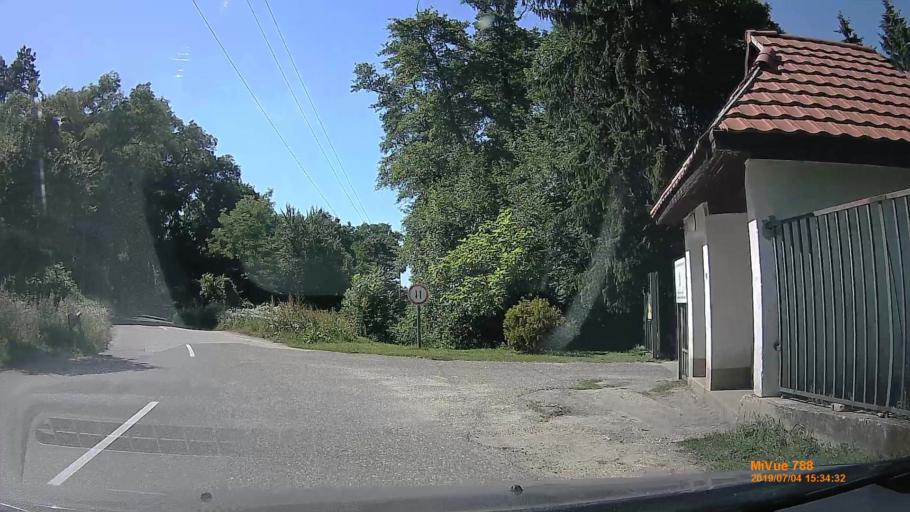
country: HU
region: Komarom-Esztergom
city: Tatabanya
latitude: 47.5390
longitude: 18.3887
